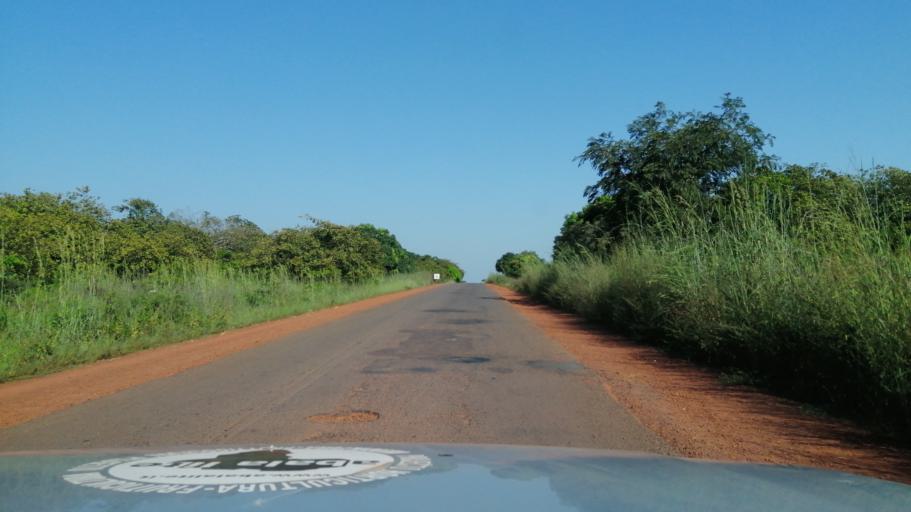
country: GW
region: Bissau
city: Bissau
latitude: 11.9588
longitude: -15.5235
